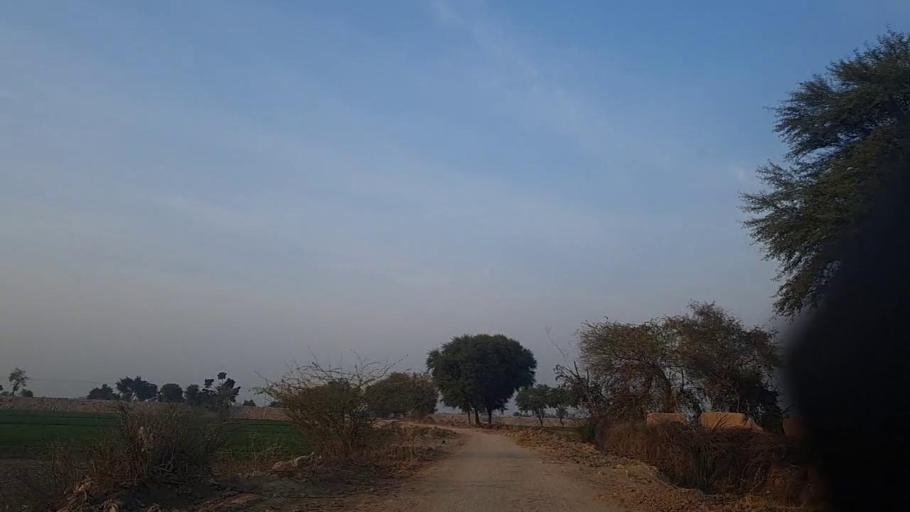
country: PK
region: Sindh
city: Sakrand
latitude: 26.1368
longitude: 68.2255
